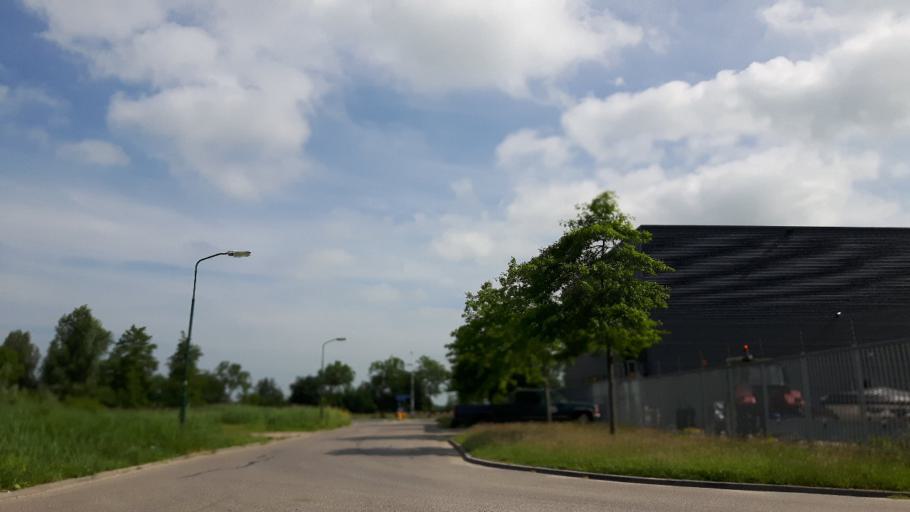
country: NL
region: Utrecht
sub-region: Gemeente De Ronde Venen
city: Mijdrecht
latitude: 52.1564
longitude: 4.8694
